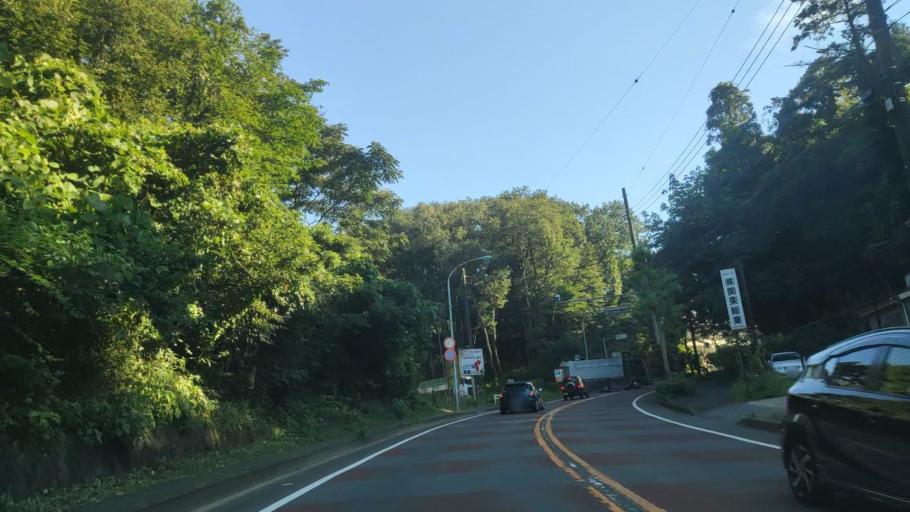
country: JP
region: Tokyo
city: Hachioji
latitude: 35.6145
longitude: 139.3151
